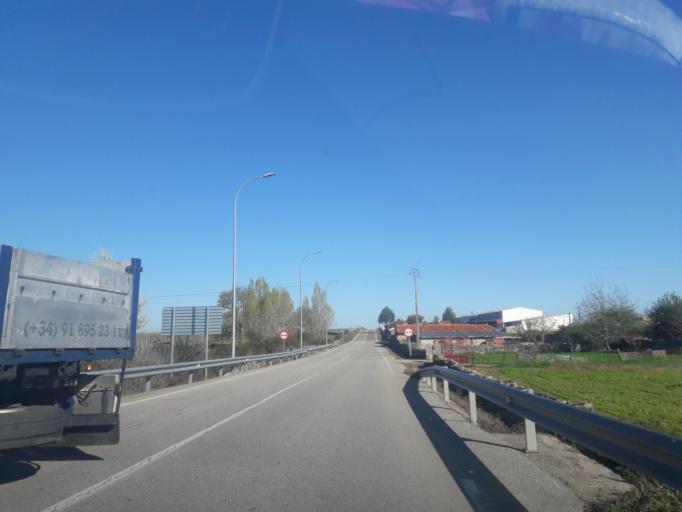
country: ES
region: Castille and Leon
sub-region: Provincia de Salamanca
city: Vitigudino
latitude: 41.0111
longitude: -6.4405
